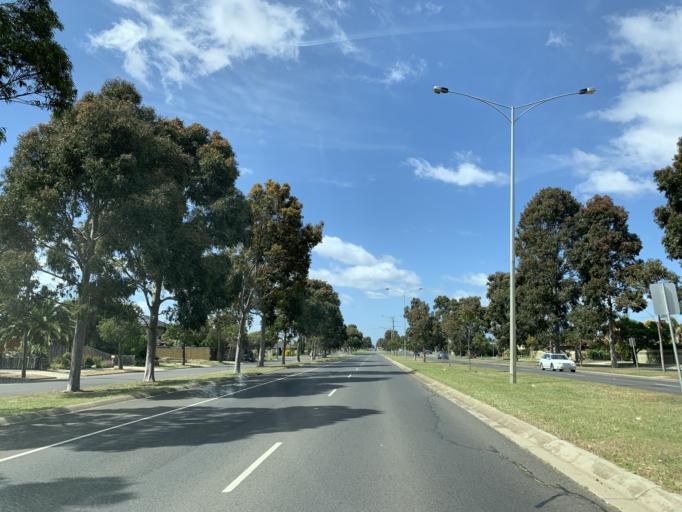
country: AU
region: Victoria
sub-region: Brimbank
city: Kealba
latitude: -37.7367
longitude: 144.8213
